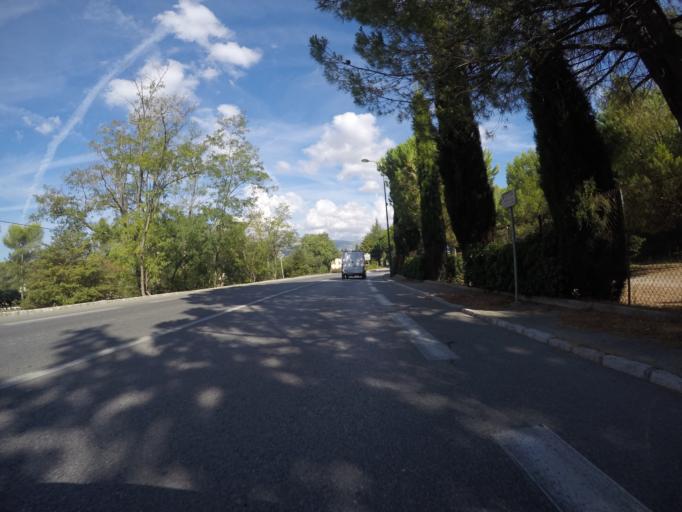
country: FR
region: Provence-Alpes-Cote d'Azur
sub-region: Departement des Alpes-Maritimes
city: Le Rouret
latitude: 43.6643
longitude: 7.0537
